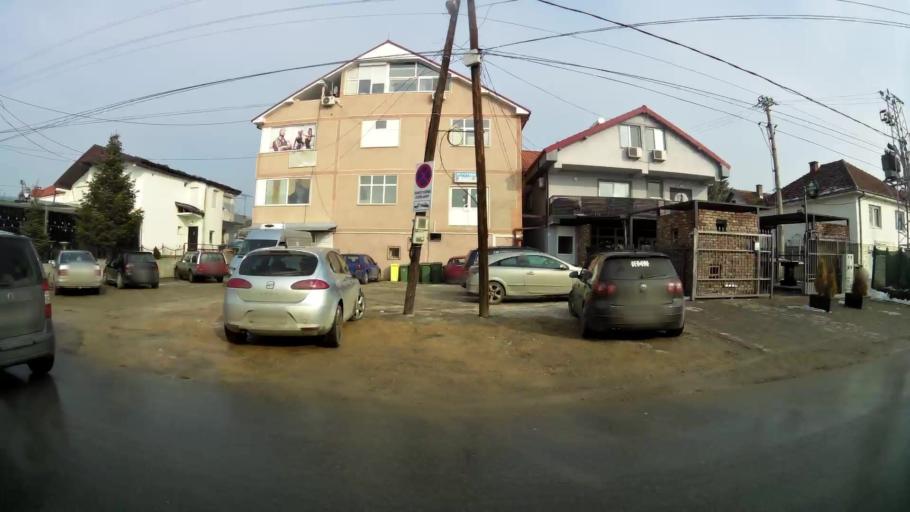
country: MK
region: Ilinden
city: Marino
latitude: 41.9908
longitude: 21.5904
